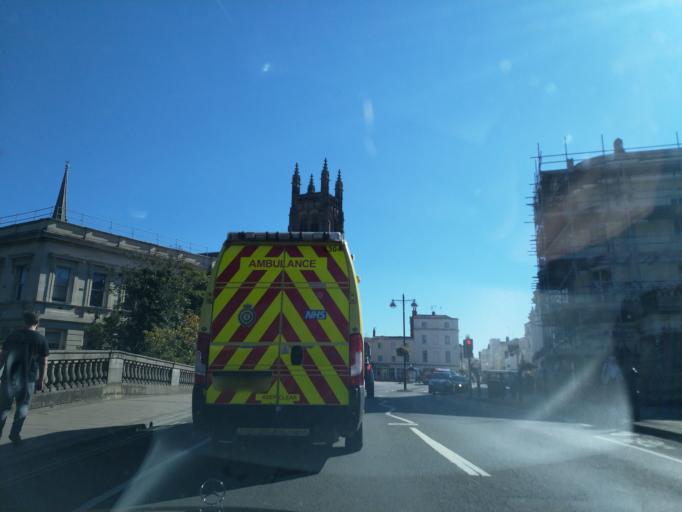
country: GB
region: England
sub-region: Warwickshire
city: Royal Leamington Spa
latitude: 52.2868
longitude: -1.5335
